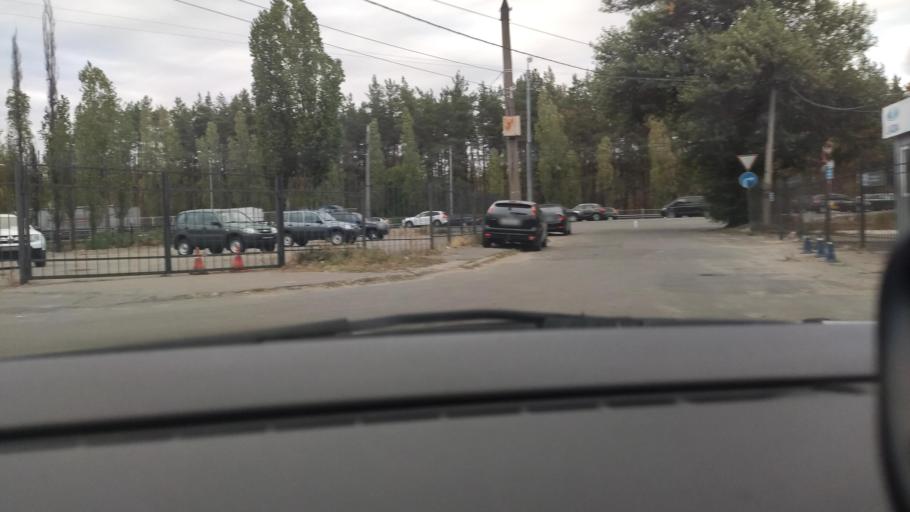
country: RU
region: Voronezj
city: Pridonskoy
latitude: 51.6472
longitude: 39.1061
